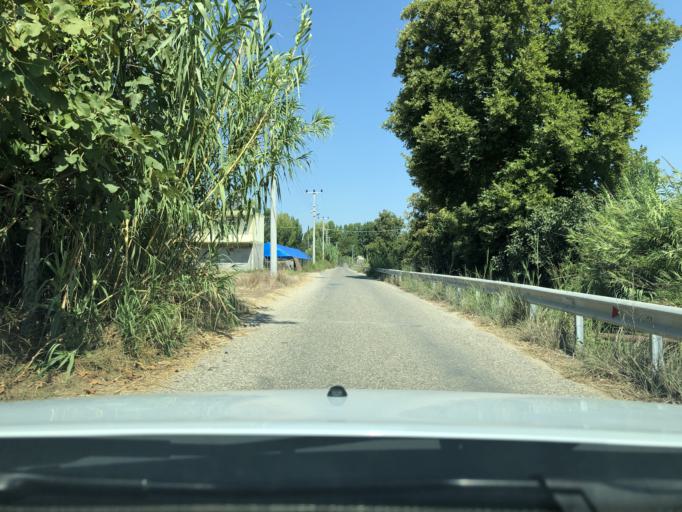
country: TR
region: Antalya
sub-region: Manavgat
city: Manavgat
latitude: 36.8054
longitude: 31.4661
